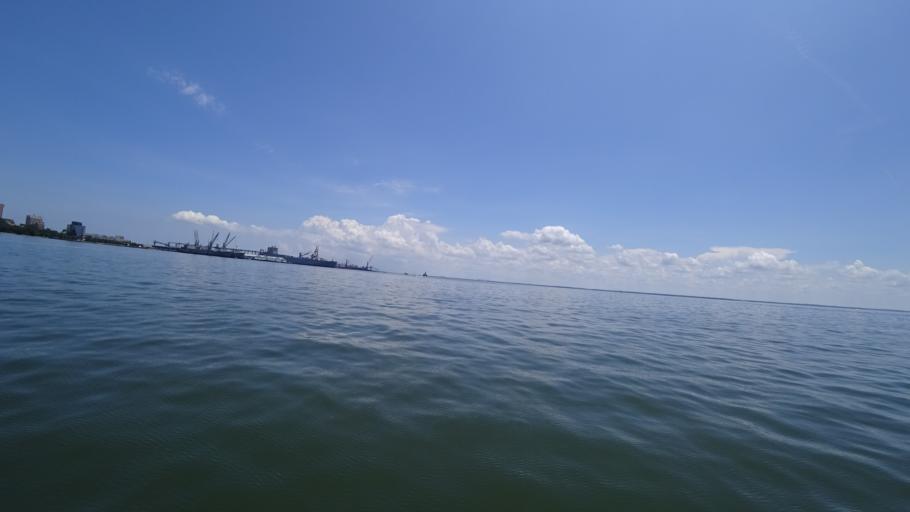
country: US
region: Virginia
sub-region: City of Newport News
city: Newport News
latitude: 36.9753
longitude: -76.4458
